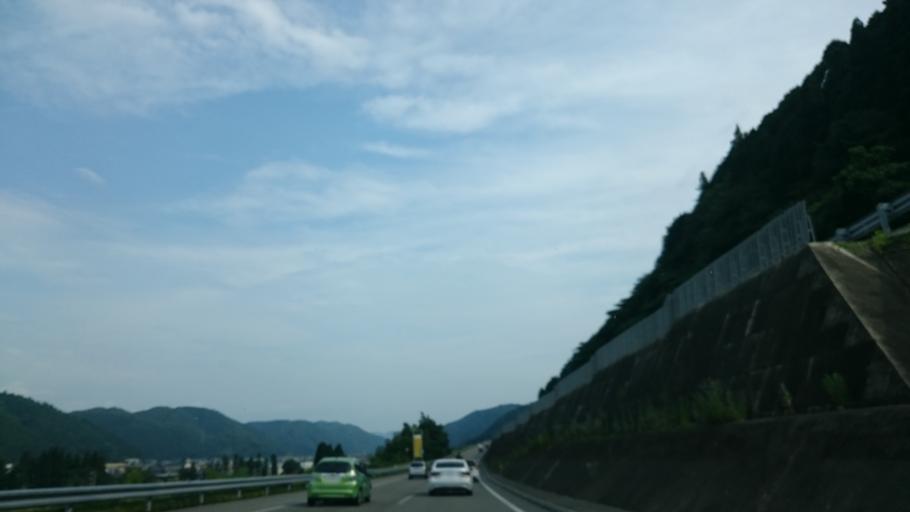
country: JP
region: Gifu
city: Gujo
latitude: 35.8270
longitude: 136.8836
